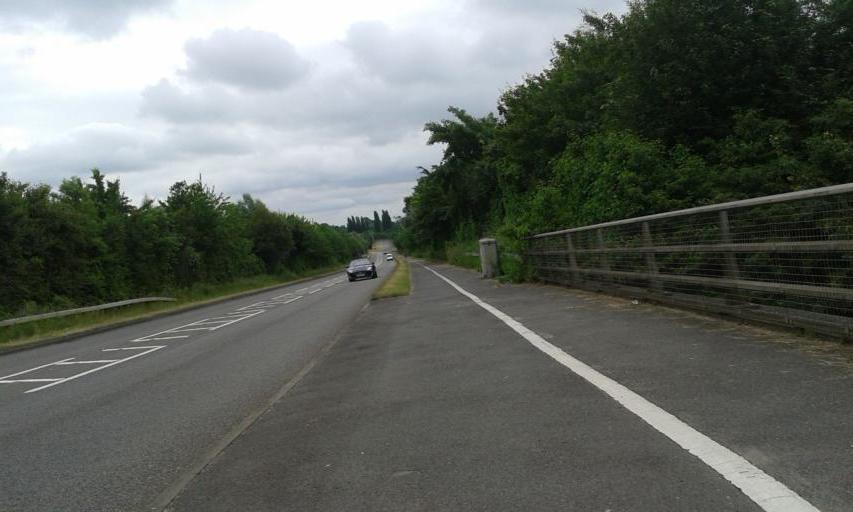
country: GB
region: England
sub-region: Leicestershire
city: Earl Shilton
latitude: 52.5597
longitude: -1.3463
